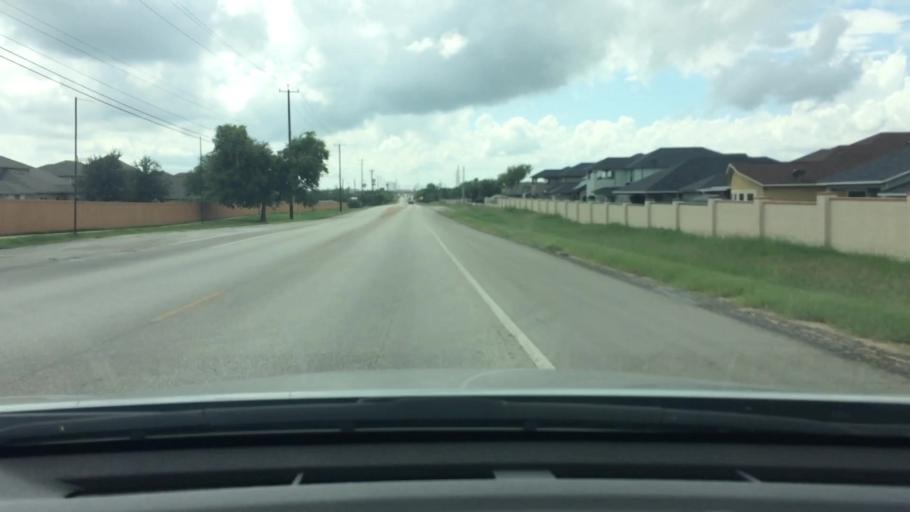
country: US
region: Texas
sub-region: Bexar County
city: Converse
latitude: 29.4677
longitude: -98.3143
